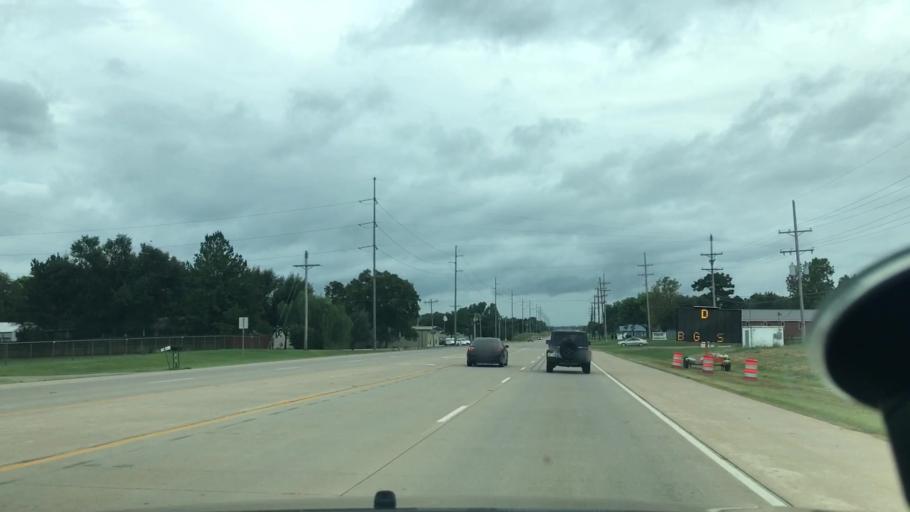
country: US
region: Oklahoma
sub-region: Seminole County
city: Seminole
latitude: 35.2624
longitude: -96.6711
